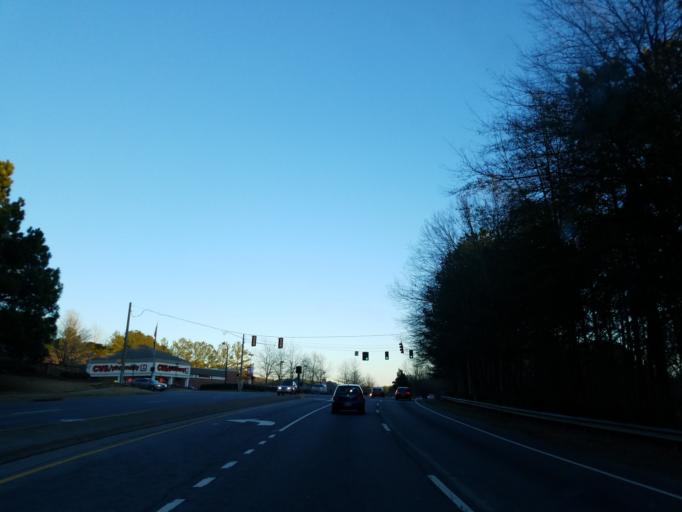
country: US
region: Georgia
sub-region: Cherokee County
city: Woodstock
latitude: 34.1065
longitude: -84.5459
